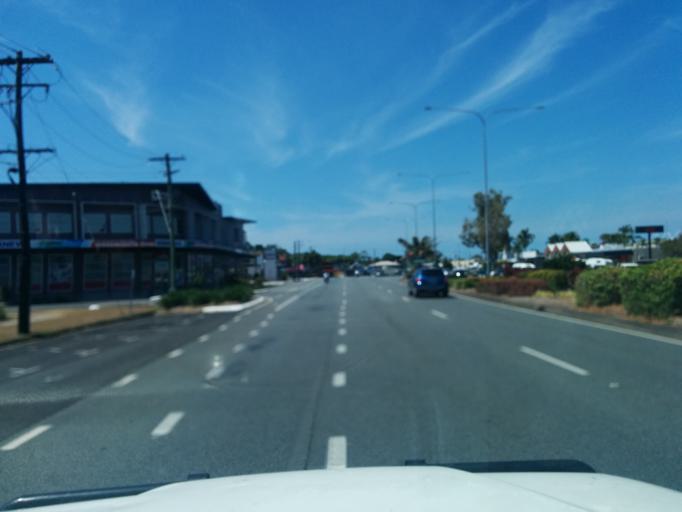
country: AU
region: Queensland
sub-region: Cairns
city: Woree
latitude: -16.9446
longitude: 145.7382
